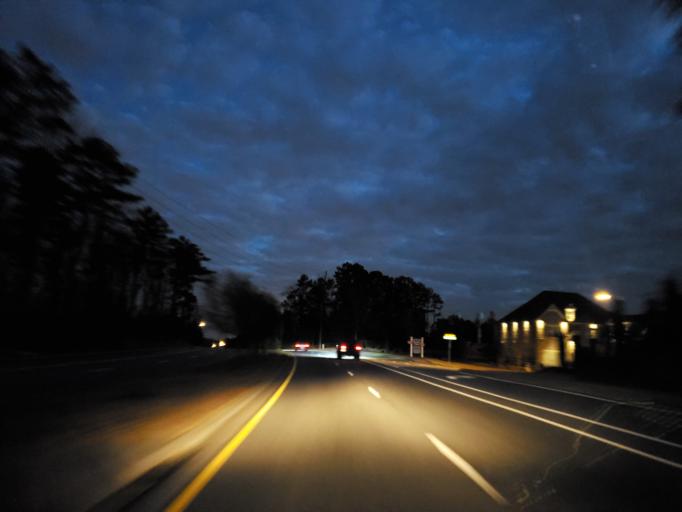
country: US
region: Georgia
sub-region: Cobb County
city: Kennesaw
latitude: 33.9903
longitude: -84.6271
